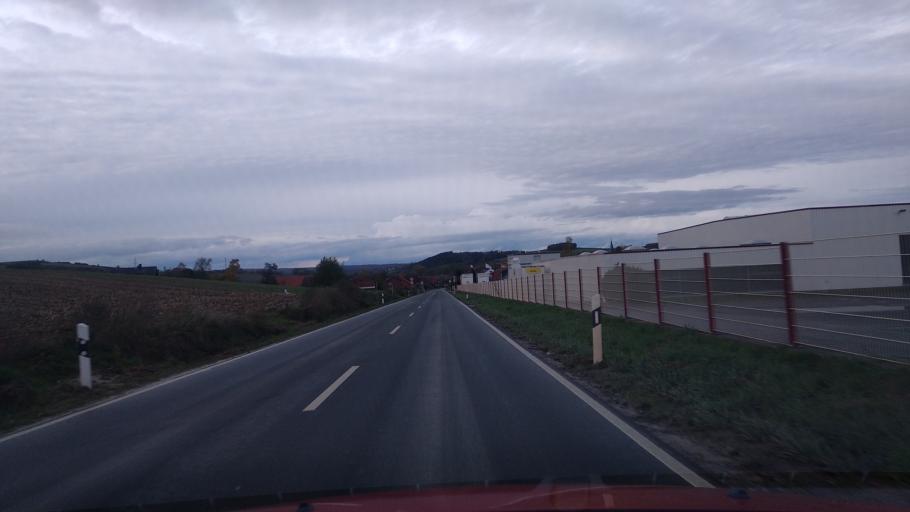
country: DE
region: North Rhine-Westphalia
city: Brakel
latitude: 51.6811
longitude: 9.2285
